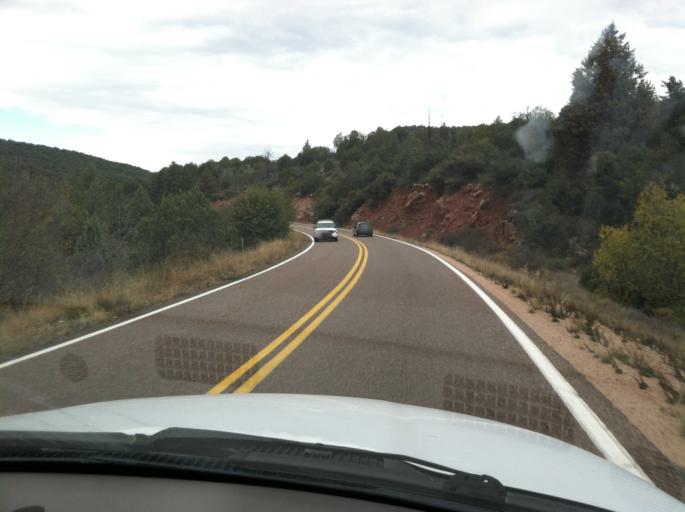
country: US
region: Arizona
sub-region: Gila County
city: Payson
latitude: 34.3128
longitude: -111.3684
